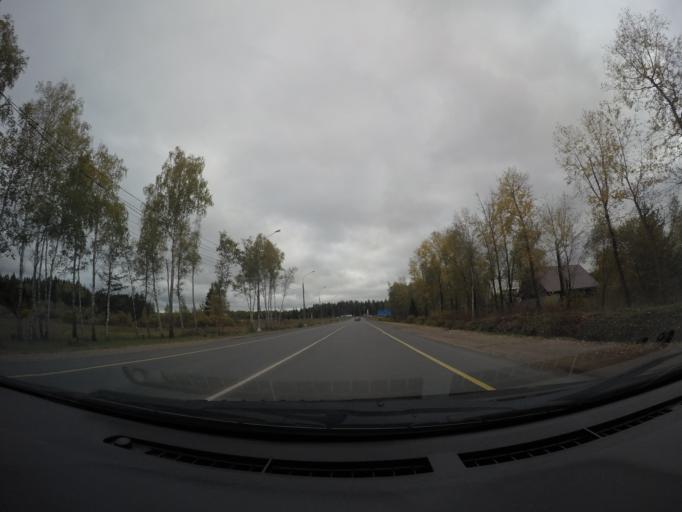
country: RU
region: Moskovskaya
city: Dorokhovo
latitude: 55.5421
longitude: 36.3958
